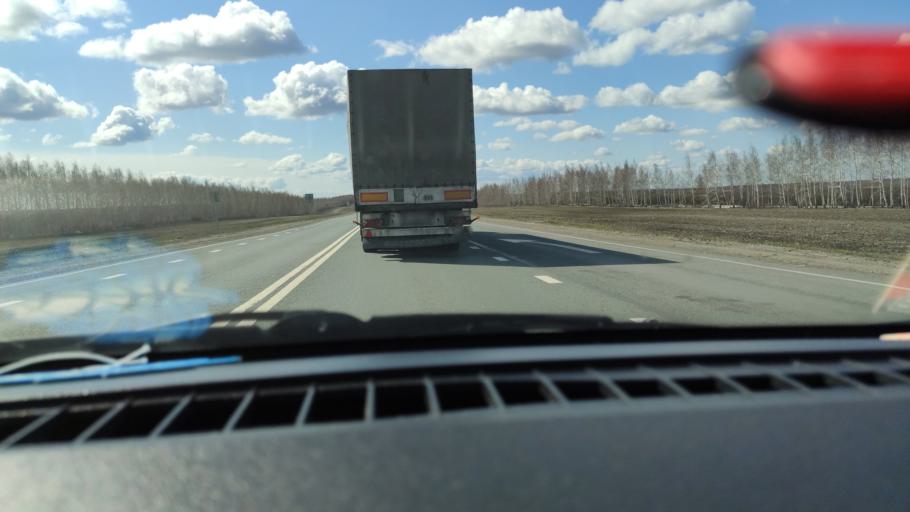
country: RU
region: Samara
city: Syzran'
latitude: 52.9163
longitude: 48.3012
